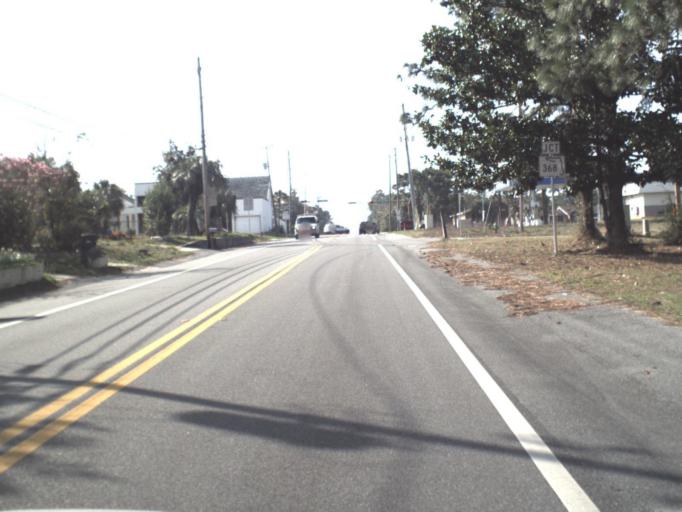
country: US
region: Florida
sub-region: Bay County
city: Pretty Bayou
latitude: 30.1913
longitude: -85.6835
